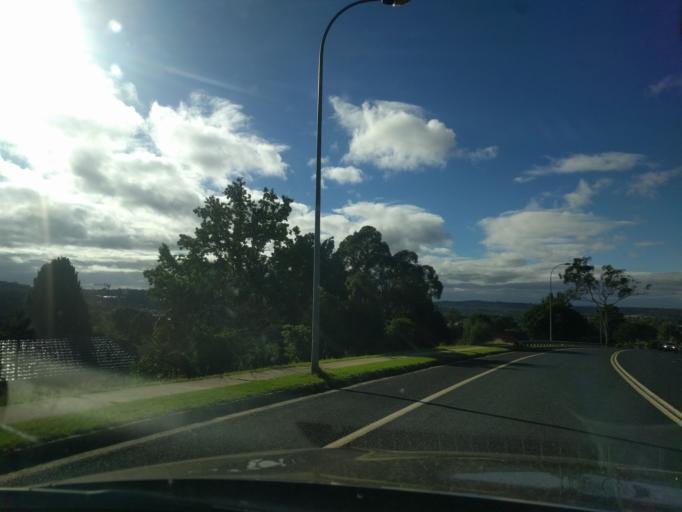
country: AU
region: New South Wales
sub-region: Armidale Dumaresq
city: Armidale
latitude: -30.4972
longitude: 151.6705
